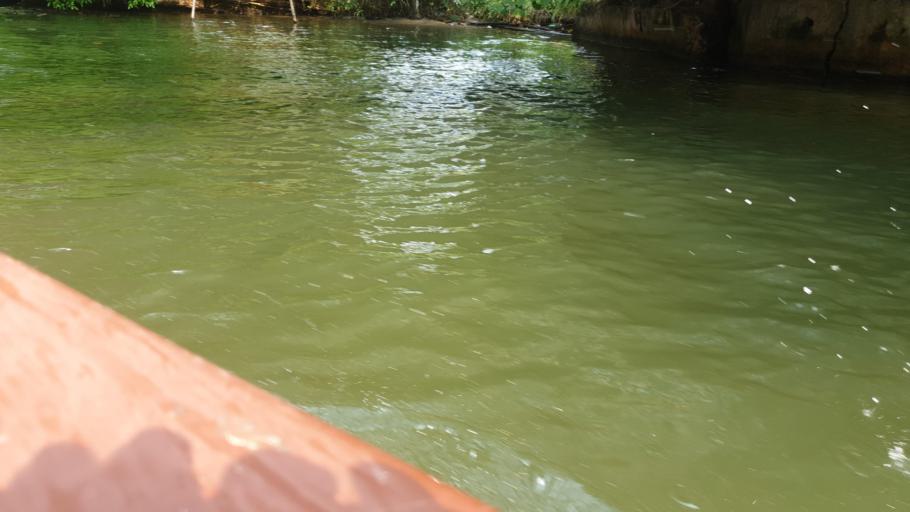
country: LK
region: Southern
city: Ambalangoda
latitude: 6.2752
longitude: 80.0431
